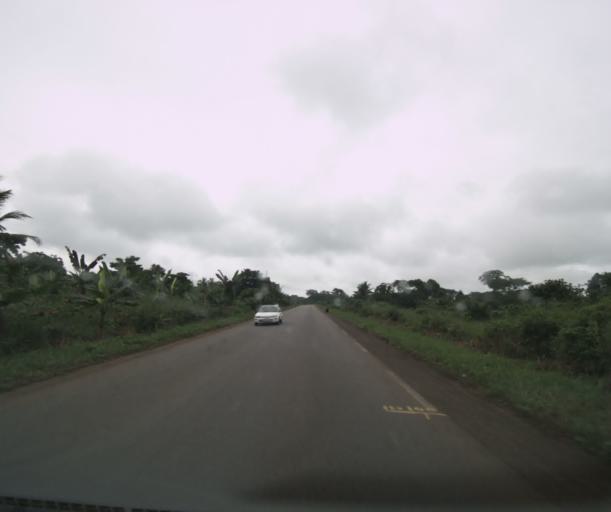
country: CM
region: Littoral
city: Edea
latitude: 3.7003
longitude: 10.1052
